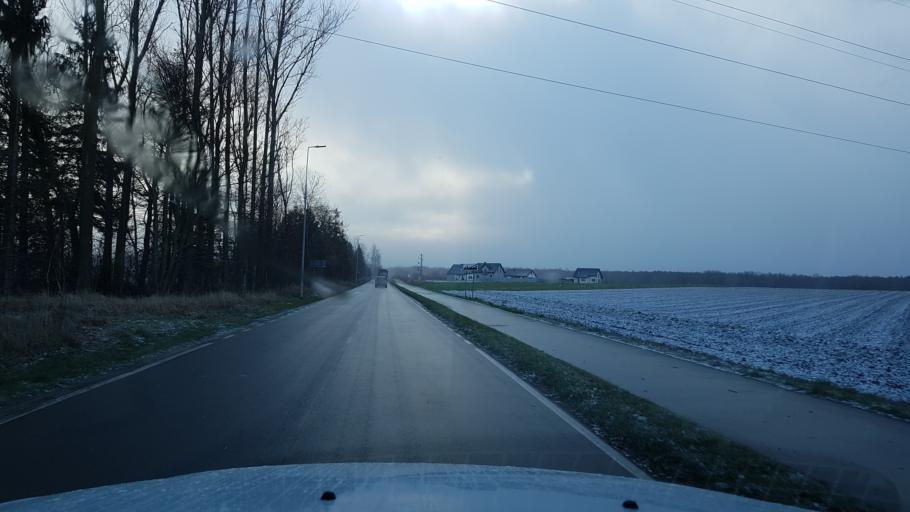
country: PL
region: West Pomeranian Voivodeship
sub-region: Powiat gryficki
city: Trzebiatow
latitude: 54.0566
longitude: 15.2986
